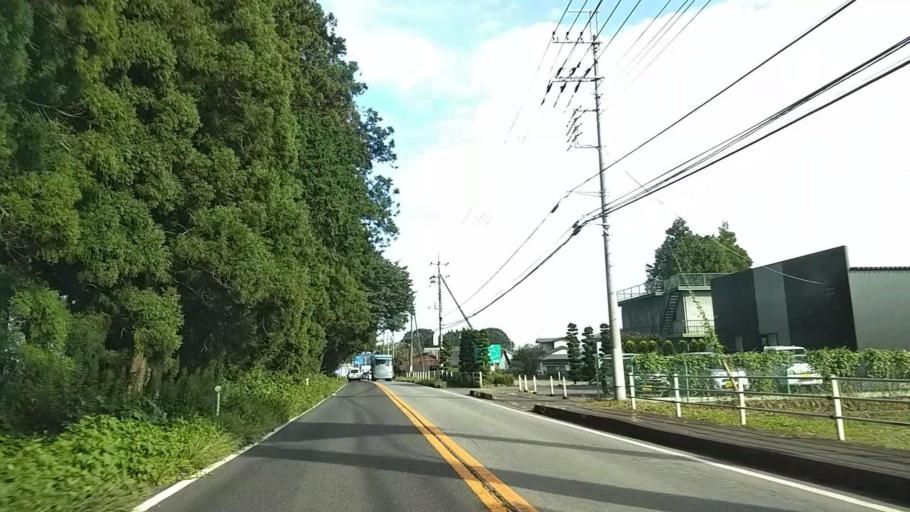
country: JP
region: Tochigi
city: Imaichi
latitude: 36.7173
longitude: 139.7159
